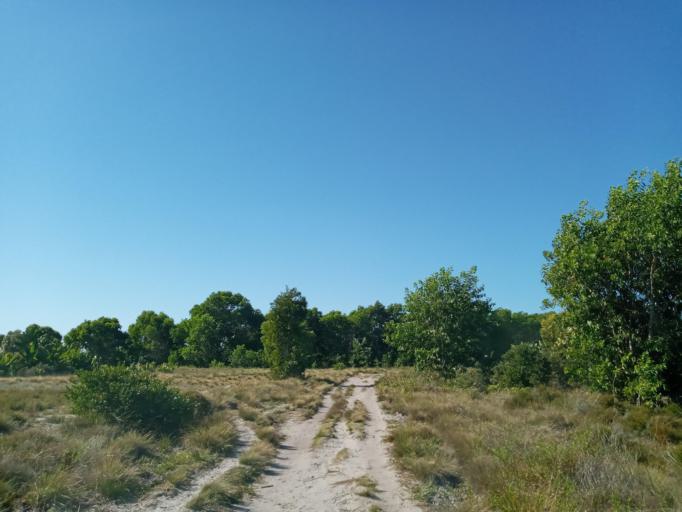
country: MG
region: Anosy
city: Fort Dauphin
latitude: -24.9054
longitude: 47.0996
